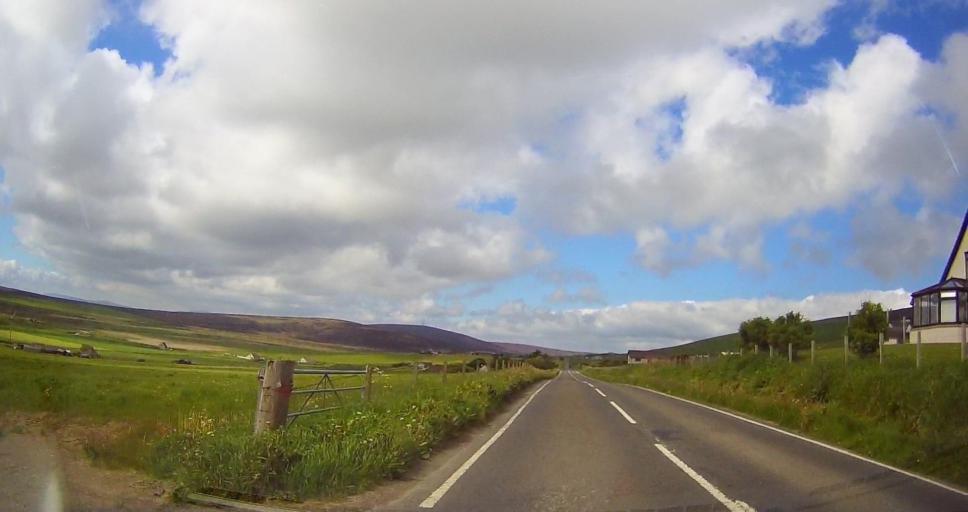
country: GB
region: Scotland
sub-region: Orkney Islands
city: Orkney
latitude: 58.9776
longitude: -3.0059
